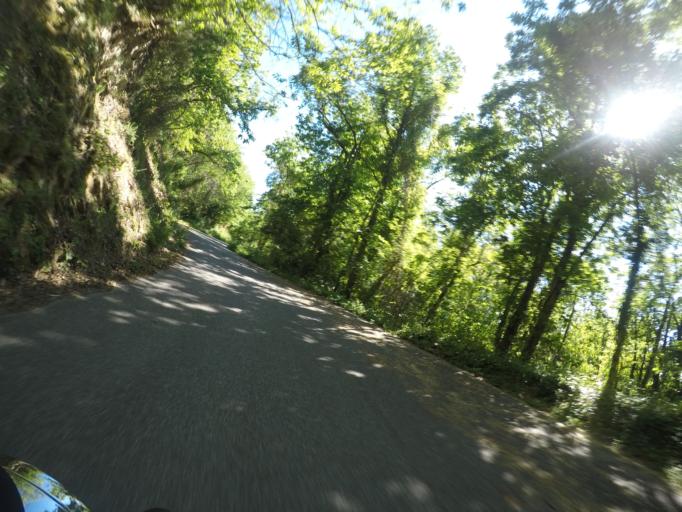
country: IT
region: Tuscany
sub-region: Provincia di Massa-Carrara
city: Fosdinovo
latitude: 44.1418
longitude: 10.0726
